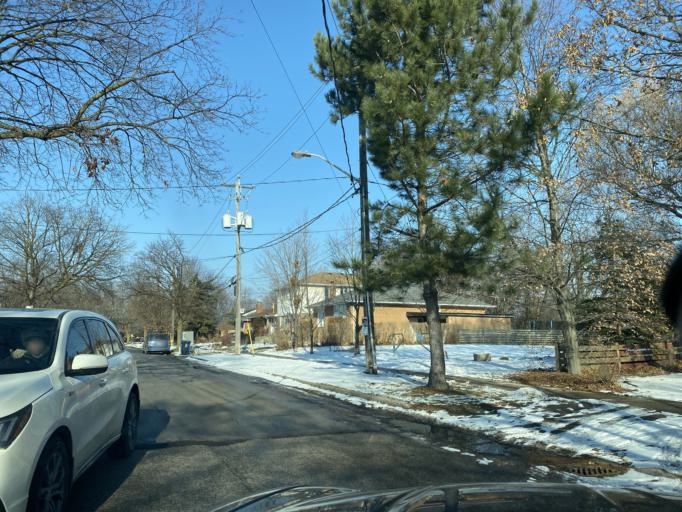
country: CA
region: Ontario
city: Etobicoke
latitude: 43.6596
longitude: -79.5634
